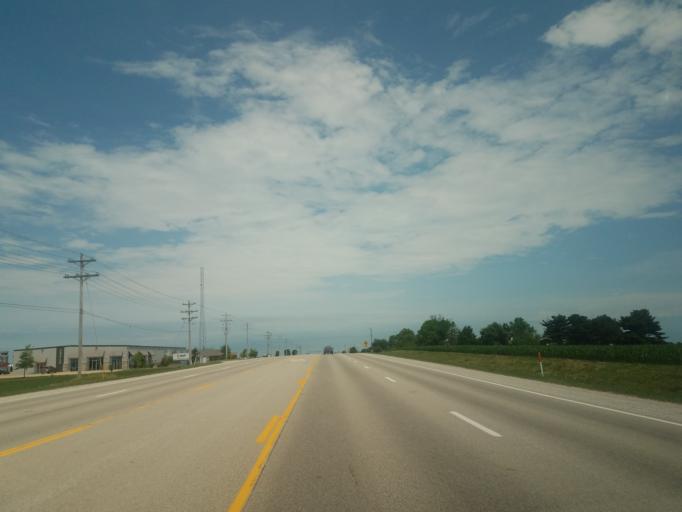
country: US
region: Illinois
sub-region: McLean County
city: Downs
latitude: 40.4665
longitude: -88.9020
